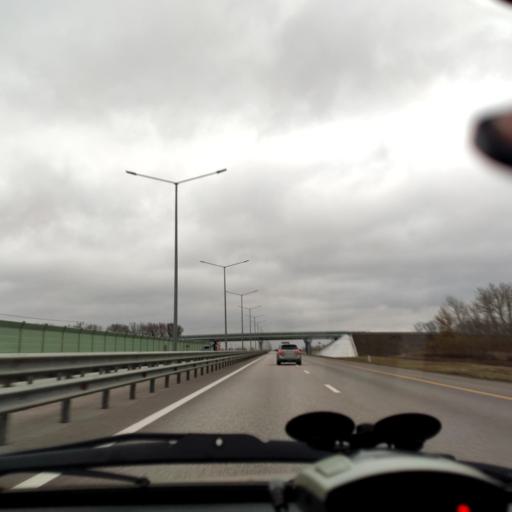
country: RU
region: Voronezj
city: Novaya Usman'
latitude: 51.5892
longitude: 39.3990
